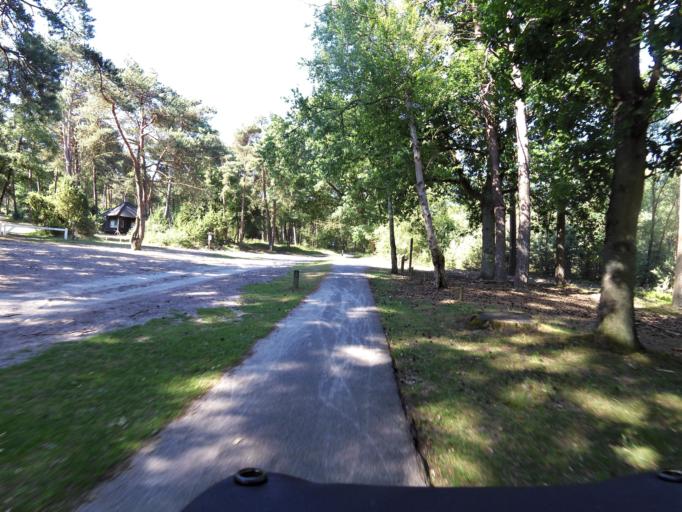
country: NL
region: Overijssel
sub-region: Gemeente Twenterand
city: Den Ham
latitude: 52.4799
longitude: 6.4116
